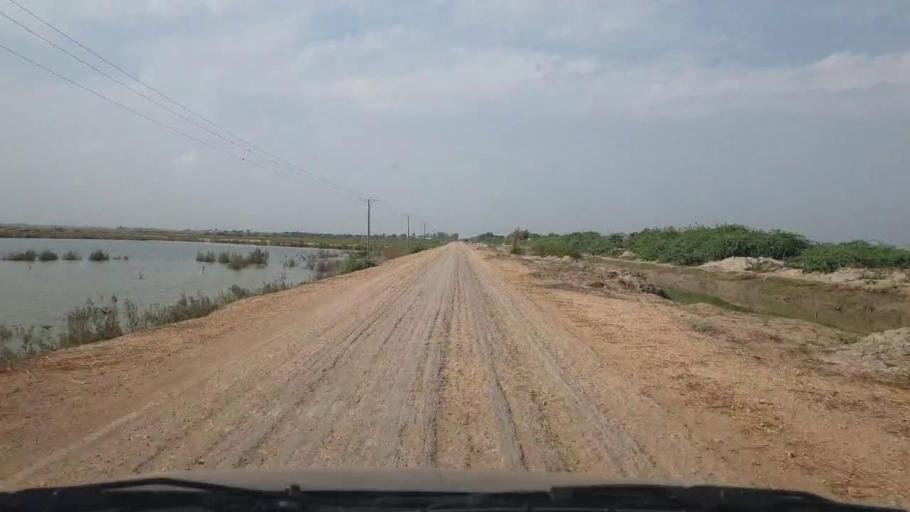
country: PK
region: Sindh
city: Kario
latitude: 24.6246
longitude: 68.5781
